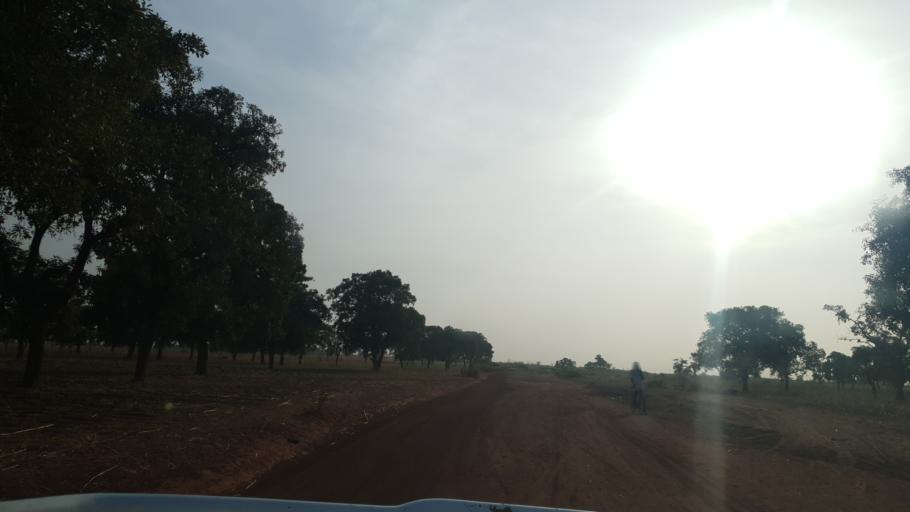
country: ML
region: Koulikoro
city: Dioila
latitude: 12.7698
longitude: -6.9275
